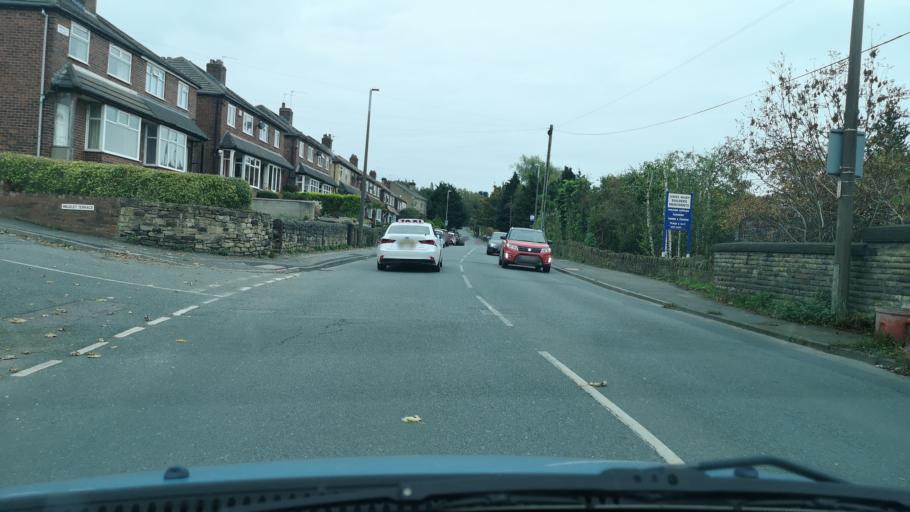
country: GB
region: England
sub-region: Kirklees
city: Heckmondwike
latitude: 53.7025
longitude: -1.6679
